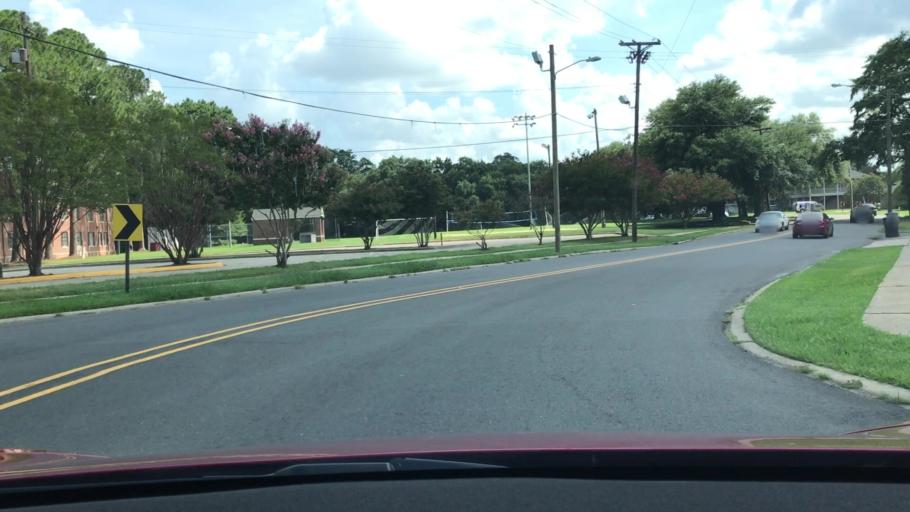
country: US
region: Louisiana
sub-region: Bossier Parish
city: Bossier City
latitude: 32.4858
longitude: -93.7332
